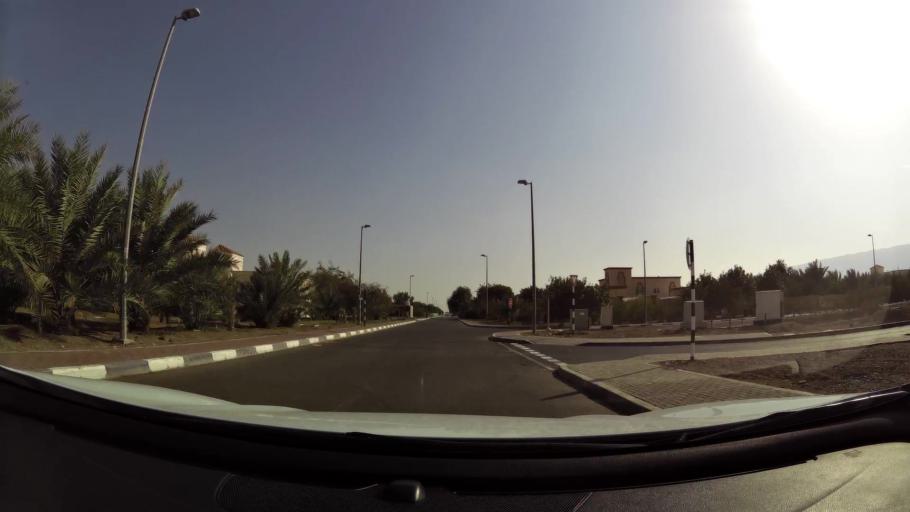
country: AE
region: Abu Dhabi
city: Al Ain
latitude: 24.0746
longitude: 55.8631
